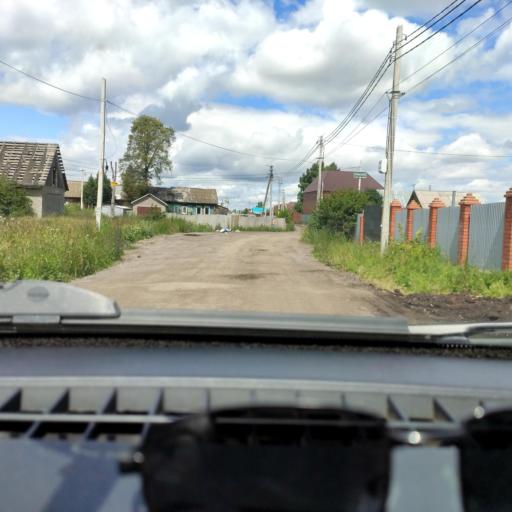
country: RU
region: Bashkortostan
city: Ufa
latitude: 54.6742
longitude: 56.0930
